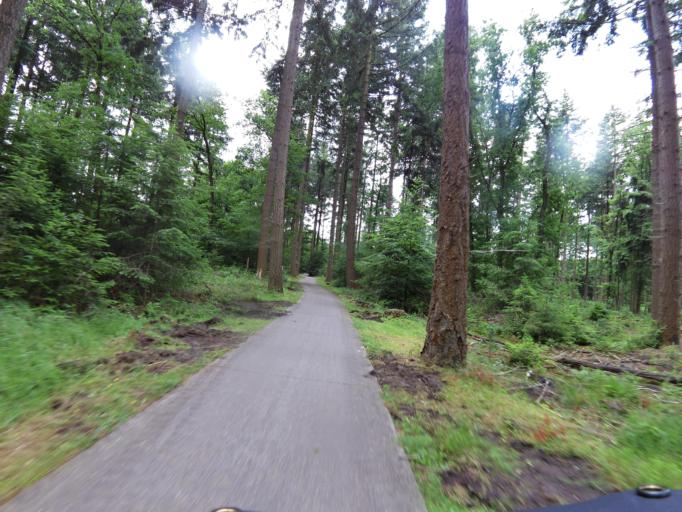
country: NL
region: Gelderland
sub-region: Gemeente Apeldoorn
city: Uddel
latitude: 52.3025
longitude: 5.8060
